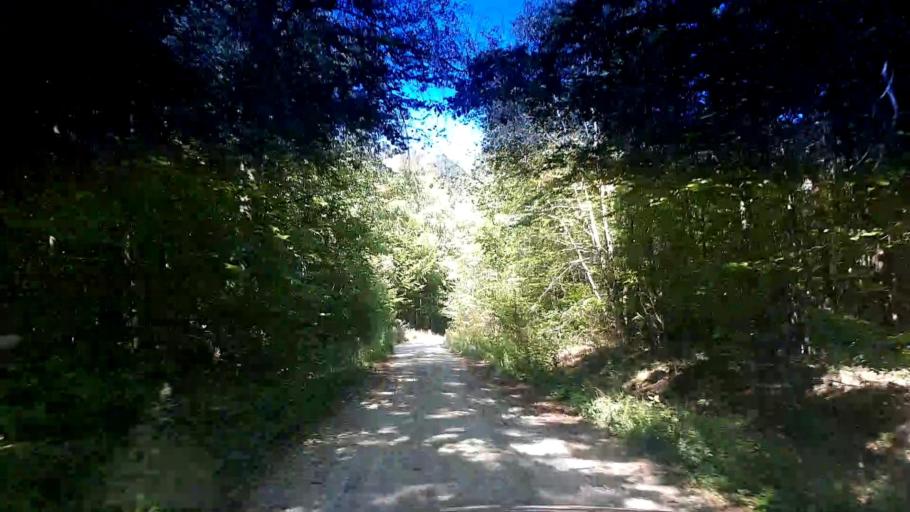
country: DE
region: Bavaria
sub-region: Upper Franconia
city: Litzendorf
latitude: 49.8941
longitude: 11.0205
